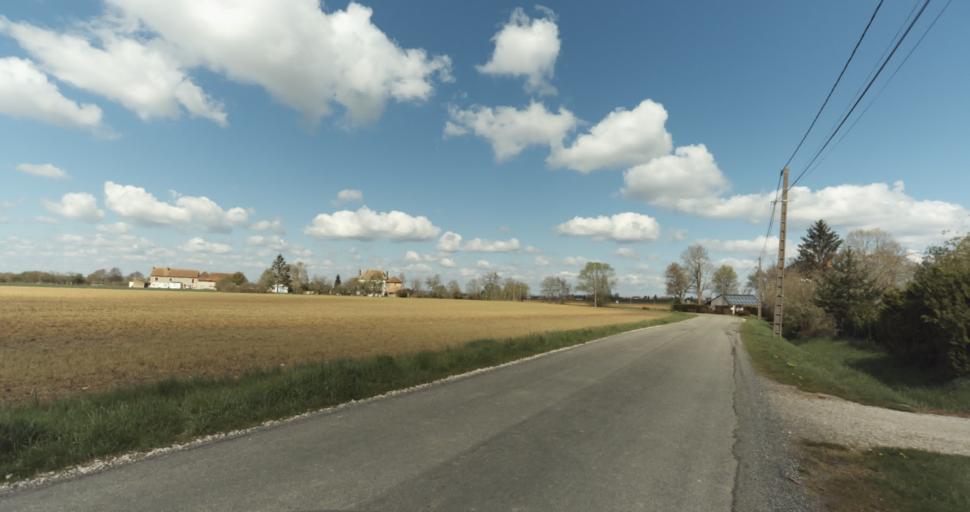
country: FR
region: Bourgogne
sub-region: Departement de la Cote-d'Or
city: Auxonne
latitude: 47.2014
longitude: 5.4256
